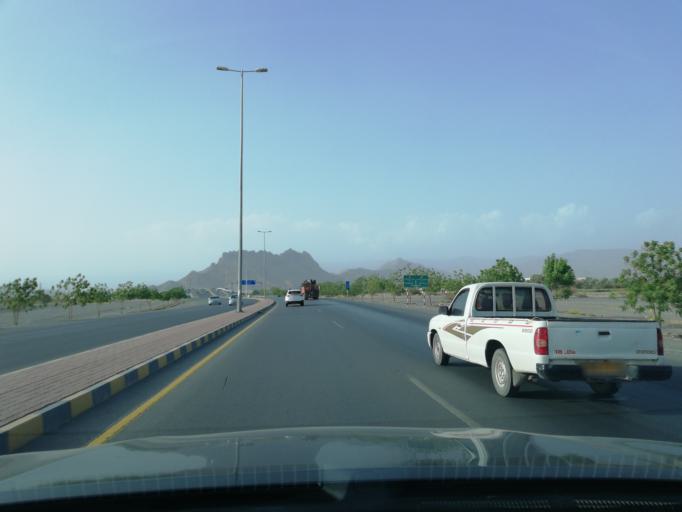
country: OM
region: Muhafazat ad Dakhiliyah
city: Nizwa
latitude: 22.8523
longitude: 57.5403
